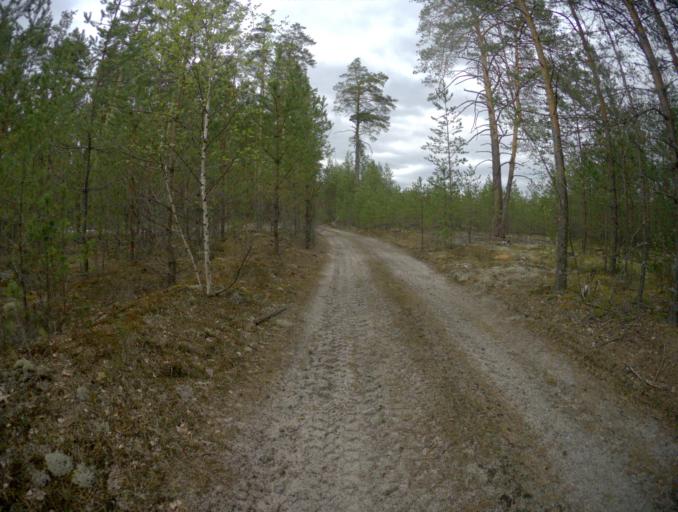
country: RU
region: Vladimir
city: Golovino
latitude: 55.8860
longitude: 40.3936
